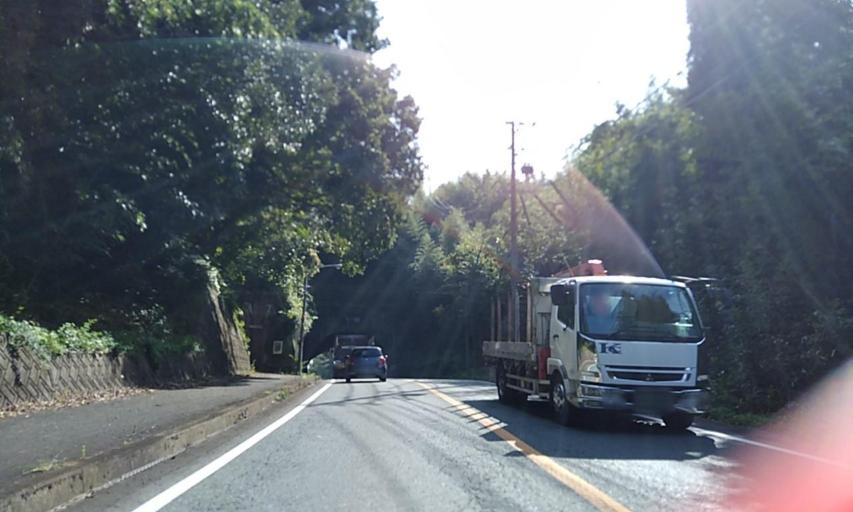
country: JP
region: Shizuoka
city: Mori
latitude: 34.8346
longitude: 137.8602
